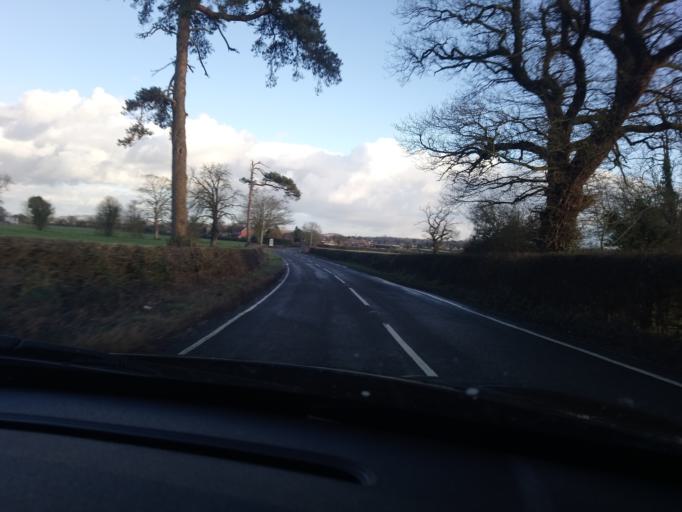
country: GB
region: England
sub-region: Shropshire
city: Wem
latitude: 52.8584
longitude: -2.7454
